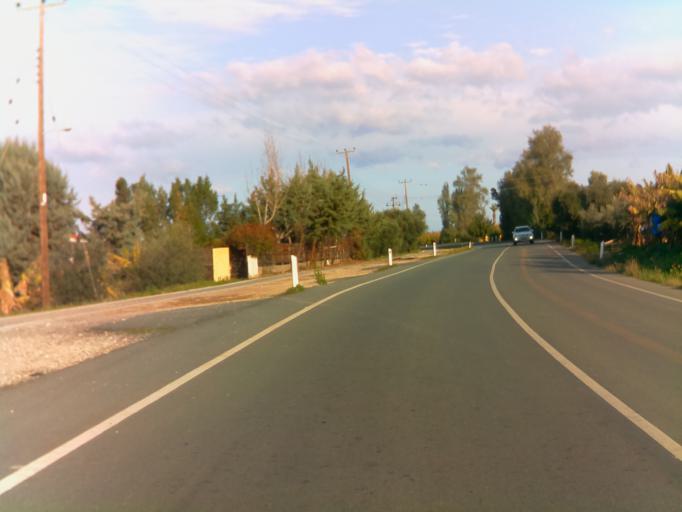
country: CY
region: Pafos
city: Pegeia
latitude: 34.8915
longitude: 32.3360
